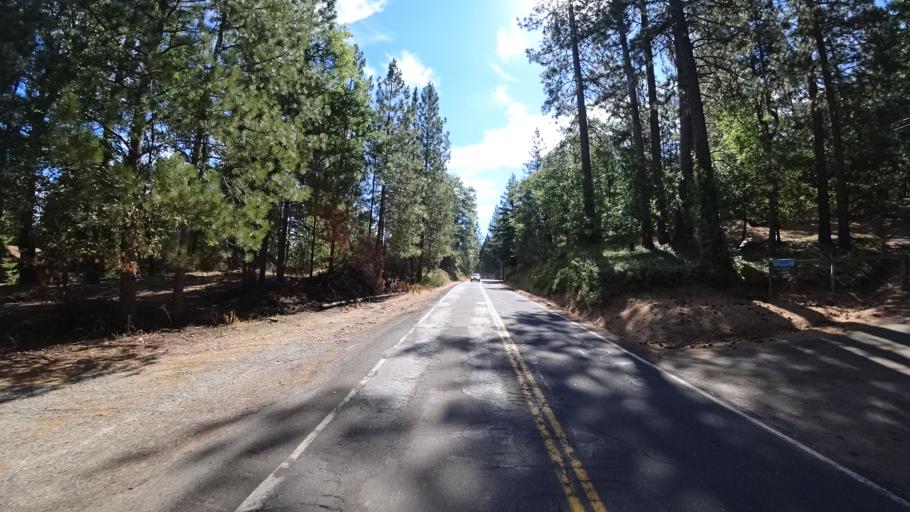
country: US
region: California
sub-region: Amador County
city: Pioneer
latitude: 38.3767
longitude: -120.4838
